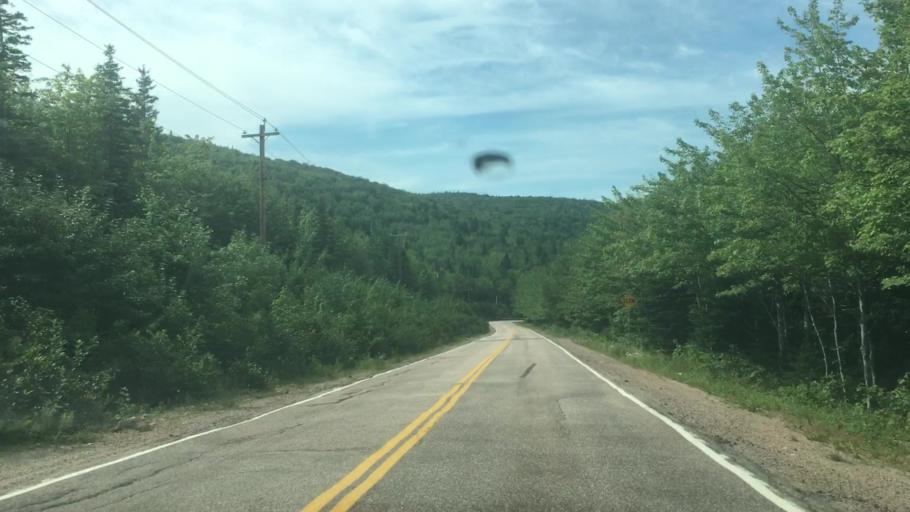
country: CA
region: Nova Scotia
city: Sydney Mines
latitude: 46.6060
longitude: -60.3933
